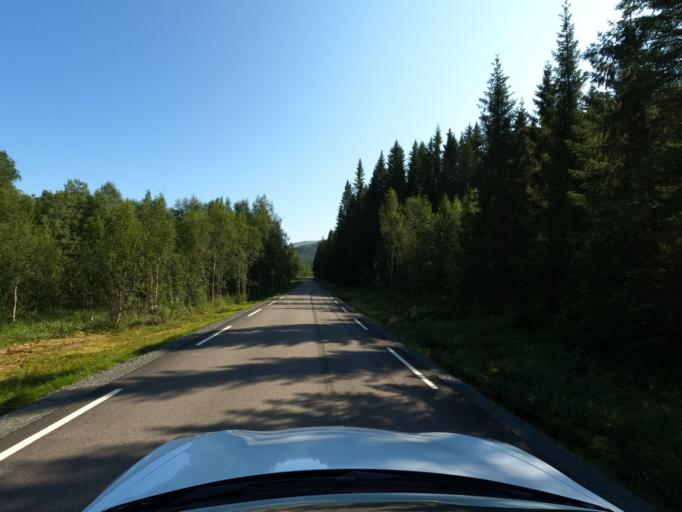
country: NO
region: Nordland
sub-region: Narvik
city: Narvik
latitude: 68.3917
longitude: 17.3378
